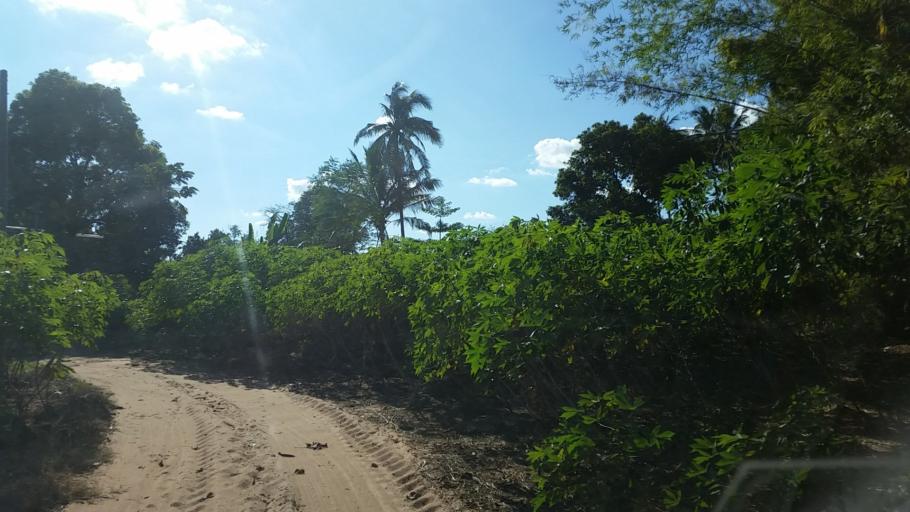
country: TH
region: Chaiyaphum
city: Thep Sathit
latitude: 15.5392
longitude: 101.4883
